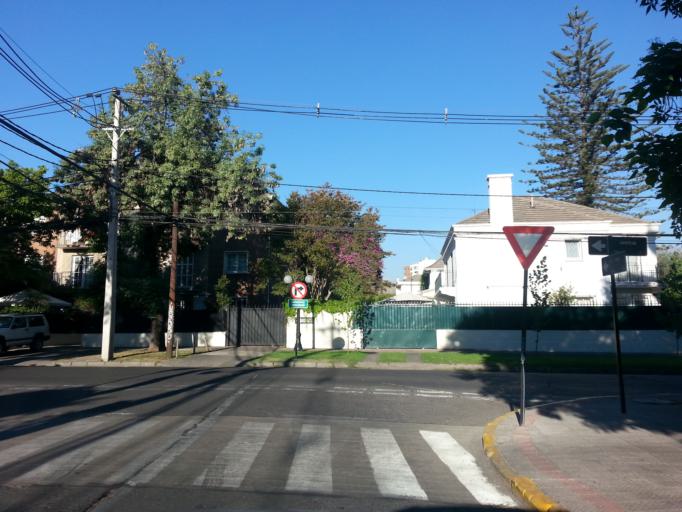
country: CL
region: Santiago Metropolitan
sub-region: Provincia de Santiago
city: Villa Presidente Frei, Nunoa, Santiago, Chile
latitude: -33.4298
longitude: -70.5912
